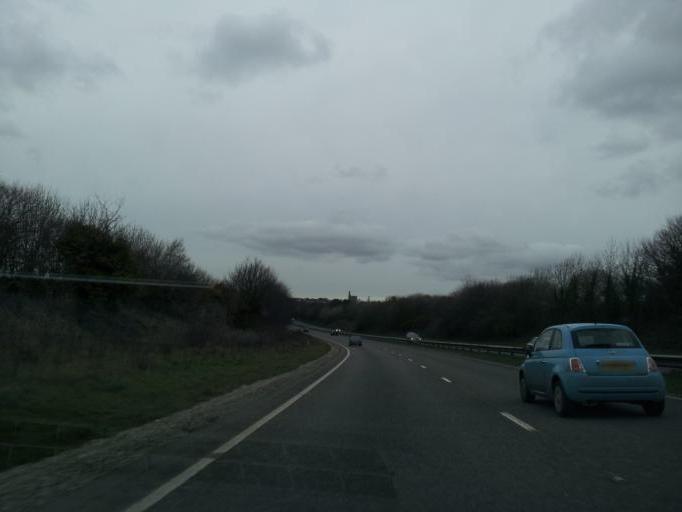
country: GB
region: England
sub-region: Cornwall
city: St. Day
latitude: 50.2530
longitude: -5.2019
